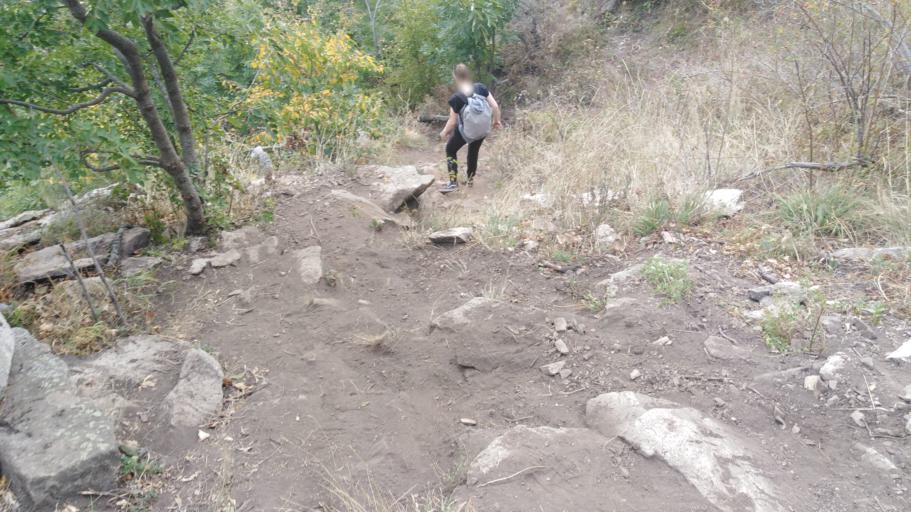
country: RU
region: Stavropol'skiy
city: Zheleznovodsk
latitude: 44.0964
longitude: 43.0275
